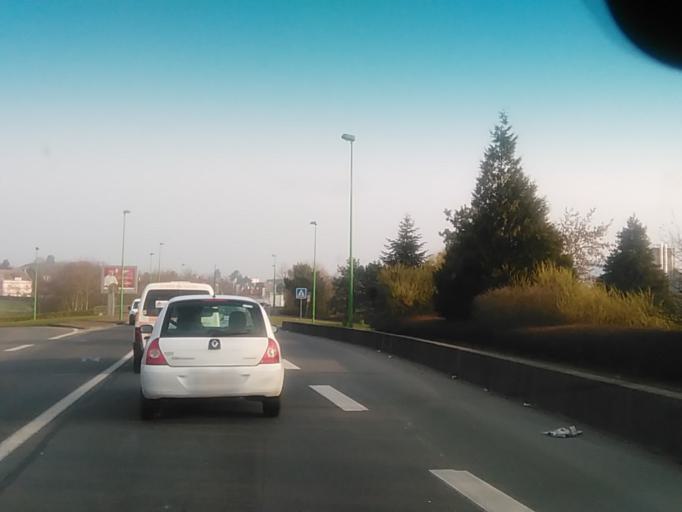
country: FR
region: Lower Normandy
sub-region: Departement du Calvados
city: Louvigny
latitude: 49.1696
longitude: -0.3845
